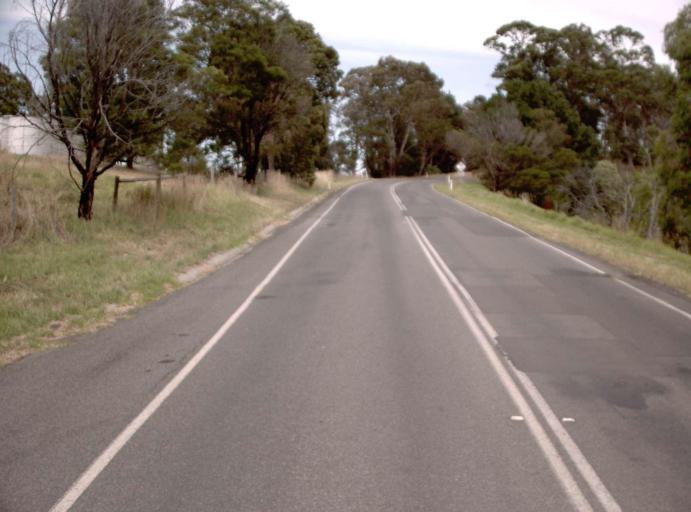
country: AU
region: Victoria
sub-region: Latrobe
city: Traralgon
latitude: -38.1377
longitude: 146.4878
